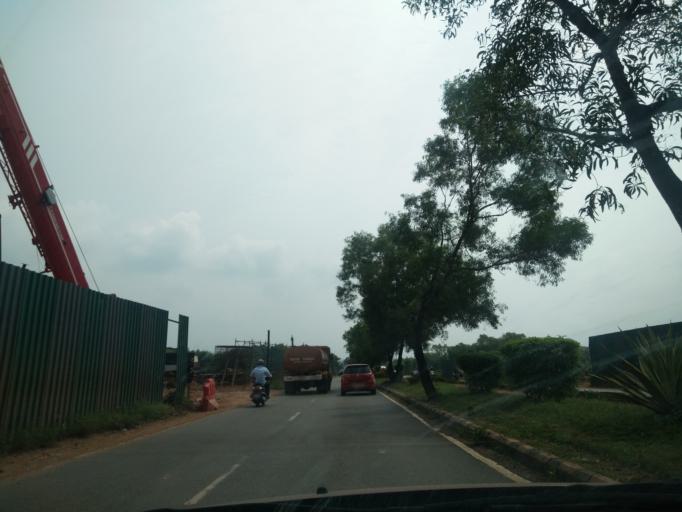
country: IN
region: Goa
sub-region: North Goa
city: Panaji
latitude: 15.4943
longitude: 73.8397
